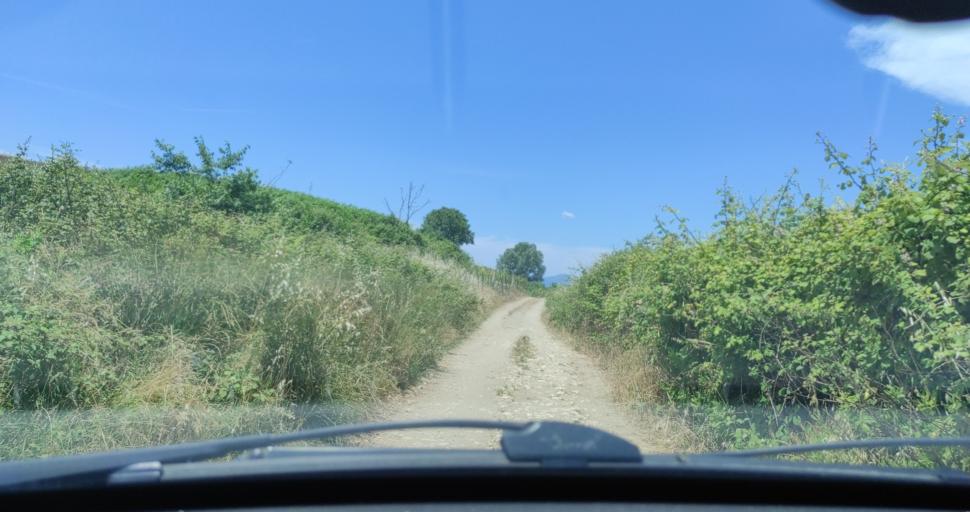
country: AL
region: Shkoder
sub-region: Rrethi i Shkodres
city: Velipoje
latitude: 41.8830
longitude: 19.3910
